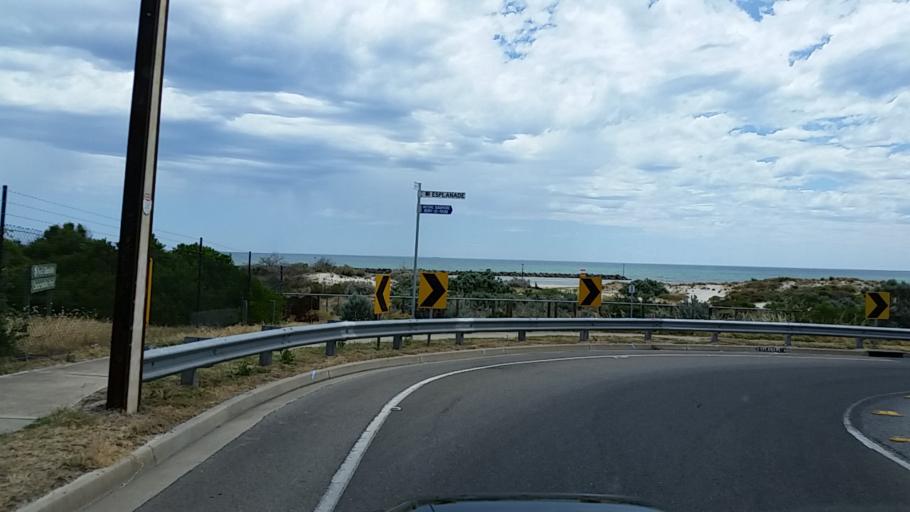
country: AU
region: South Australia
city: Port Adelaide
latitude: -34.8502
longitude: 138.4772
